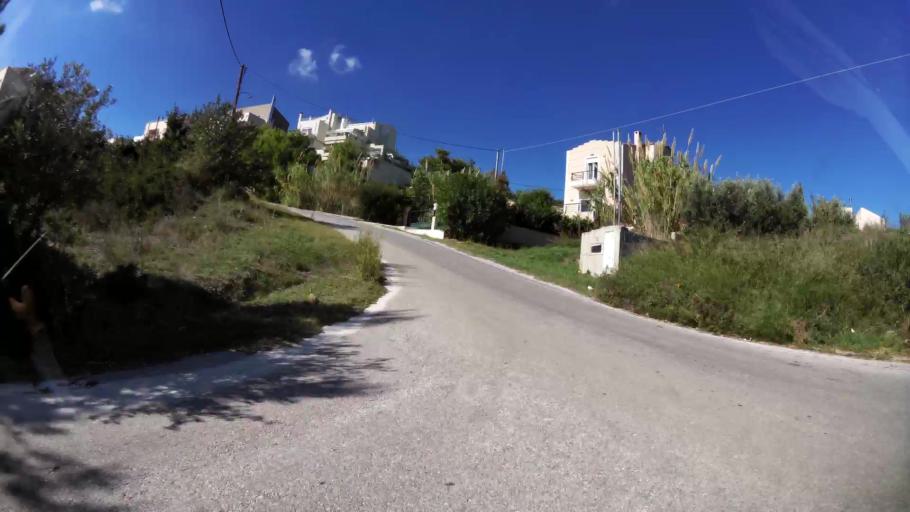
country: GR
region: Attica
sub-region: Nomarchia Anatolikis Attikis
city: Dhrafi
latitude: 38.0145
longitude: 23.9105
